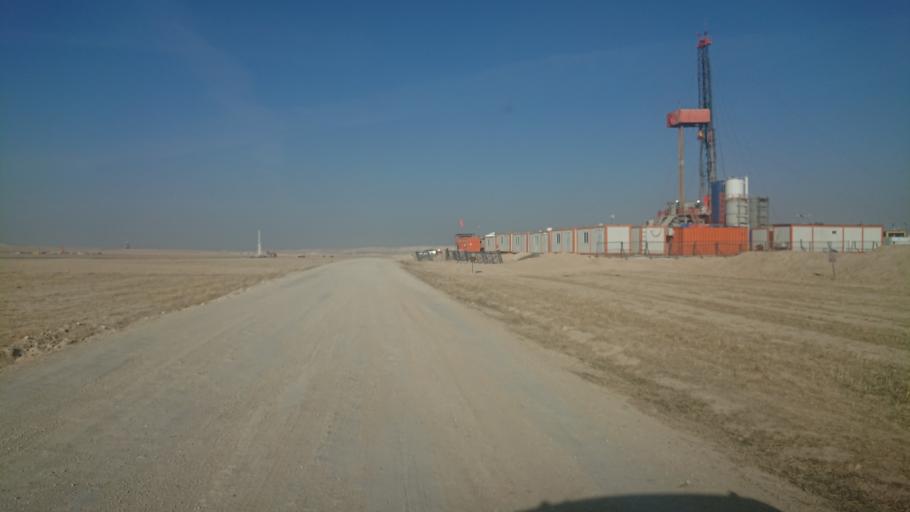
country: TR
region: Aksaray
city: Sultanhani
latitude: 38.0577
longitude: 33.6138
